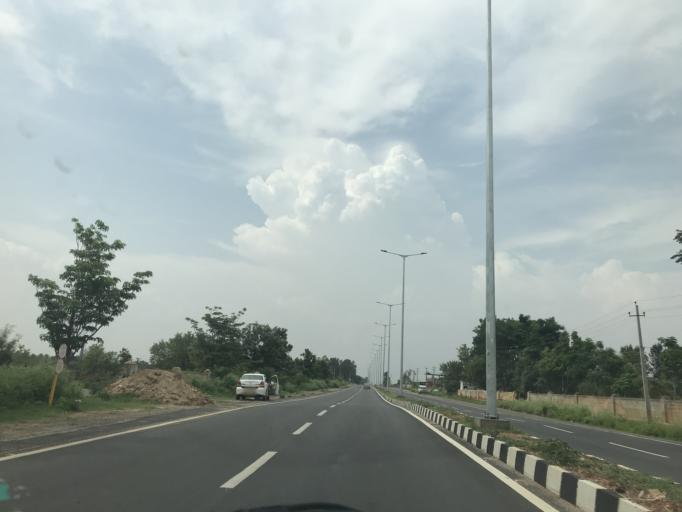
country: IN
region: Karnataka
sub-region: Bangalore Urban
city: Yelahanka
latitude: 13.1111
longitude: 77.6668
